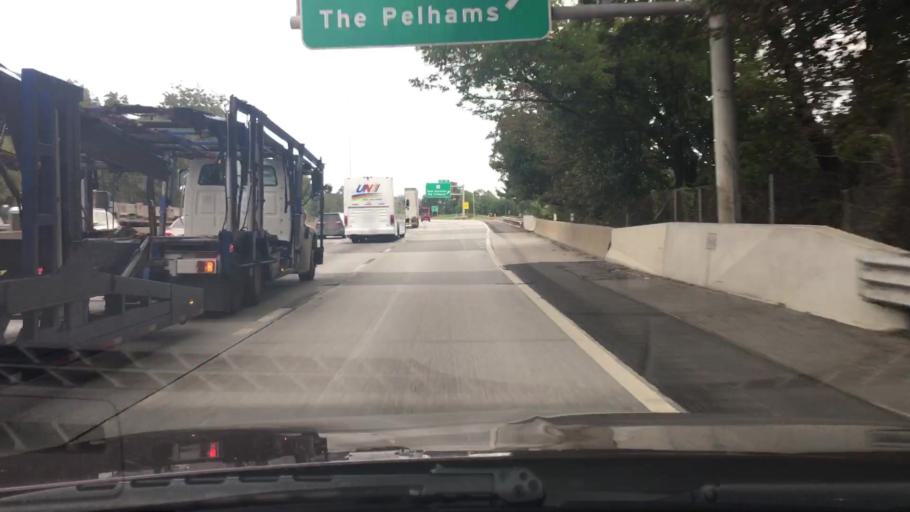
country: US
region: New York
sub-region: Westchester County
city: Pelham Manor
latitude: 40.8960
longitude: -73.7977
